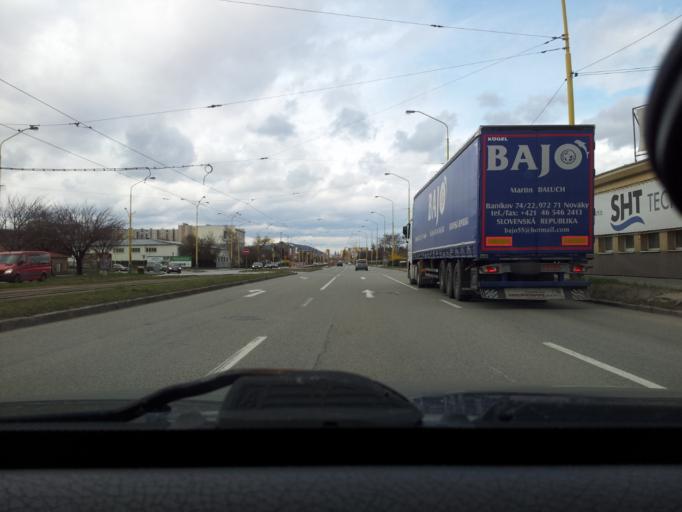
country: SK
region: Kosicky
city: Kosice
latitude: 48.6938
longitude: 21.2650
